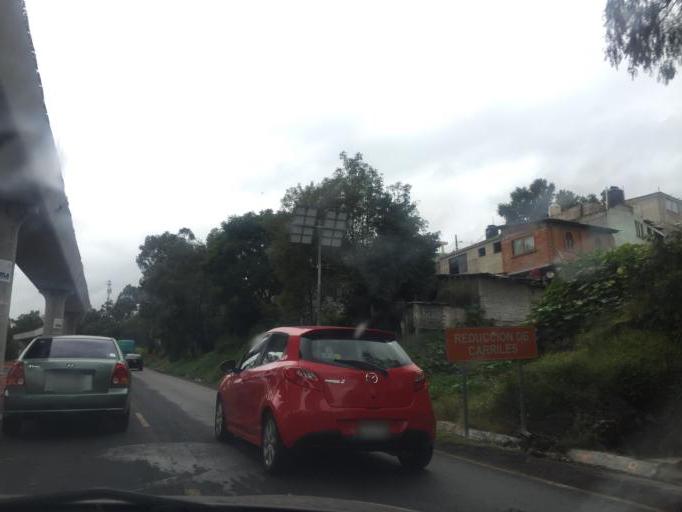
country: MX
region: Mexico City
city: Xochimilco
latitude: 19.2479
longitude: -99.1547
